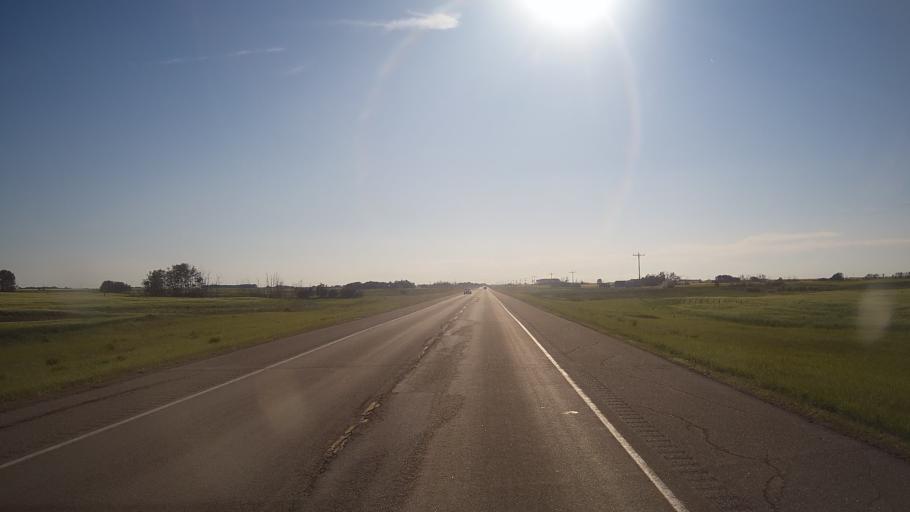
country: CA
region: Saskatchewan
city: Lanigan
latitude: 51.7944
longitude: -104.7300
